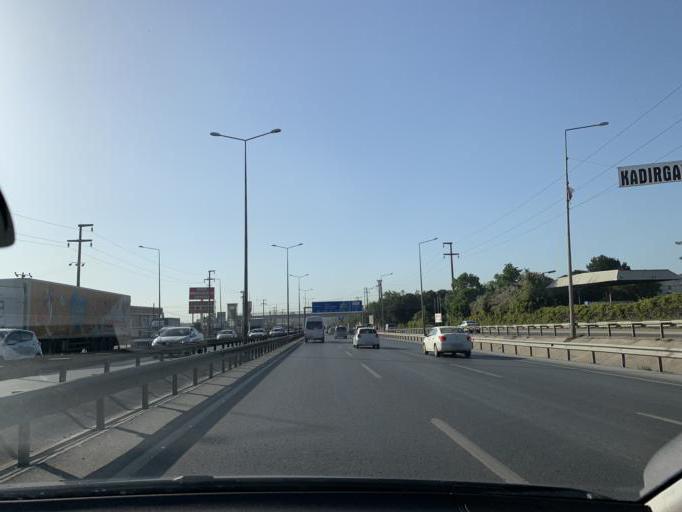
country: TR
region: Kocaeli
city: Darica
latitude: 40.7970
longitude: 29.3864
